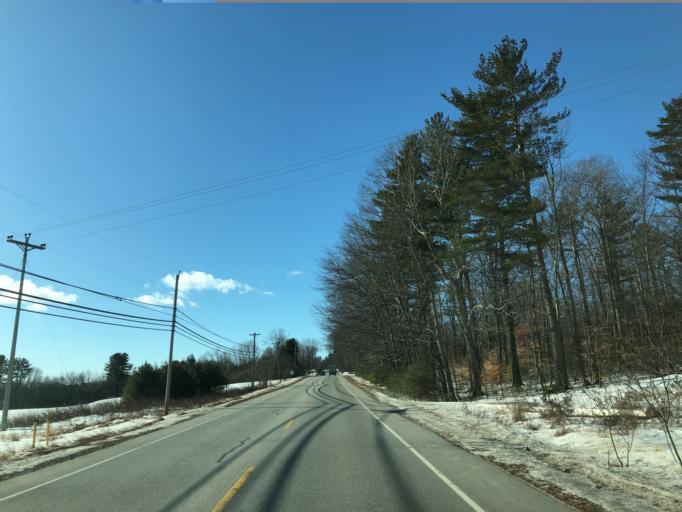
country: US
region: Maine
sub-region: Cumberland County
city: South Windham
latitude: 43.7757
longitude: -70.4177
